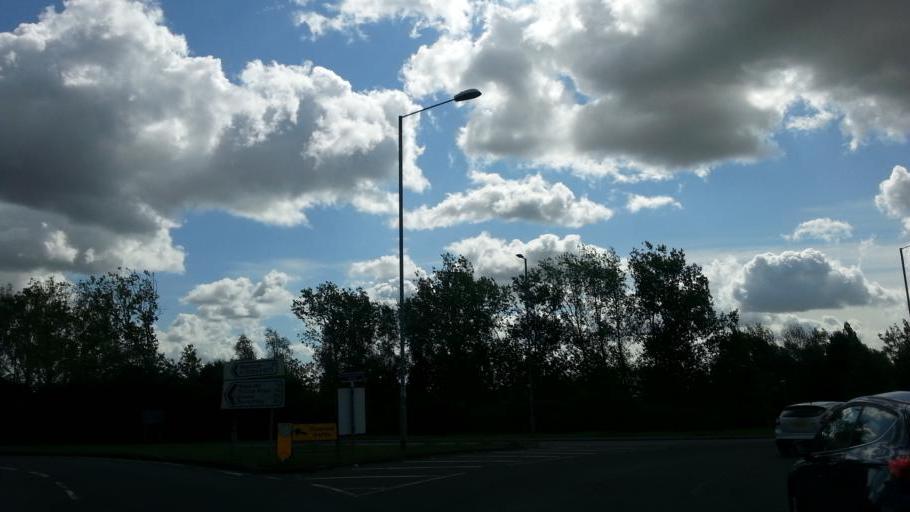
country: GB
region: England
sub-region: Essex
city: Basildon
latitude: 51.5793
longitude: 0.4436
